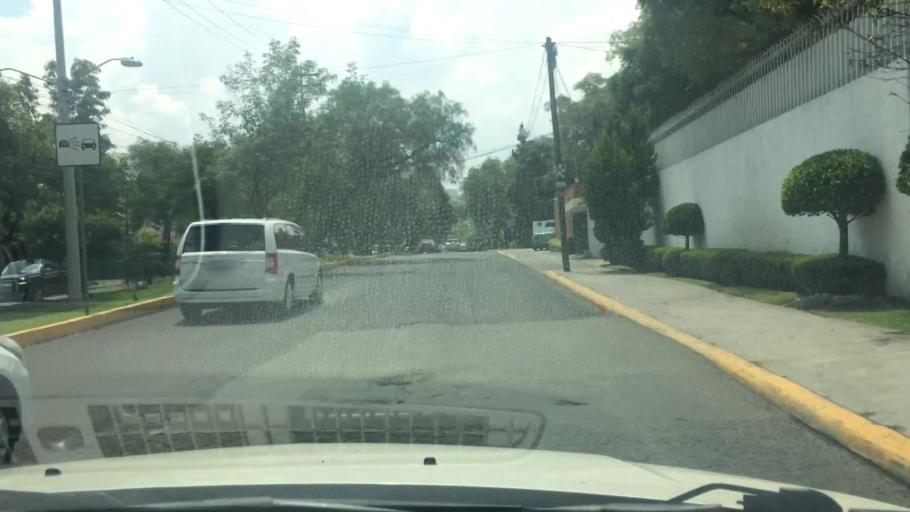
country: MX
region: Mexico City
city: Magdalena Contreras
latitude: 19.3142
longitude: -99.2027
